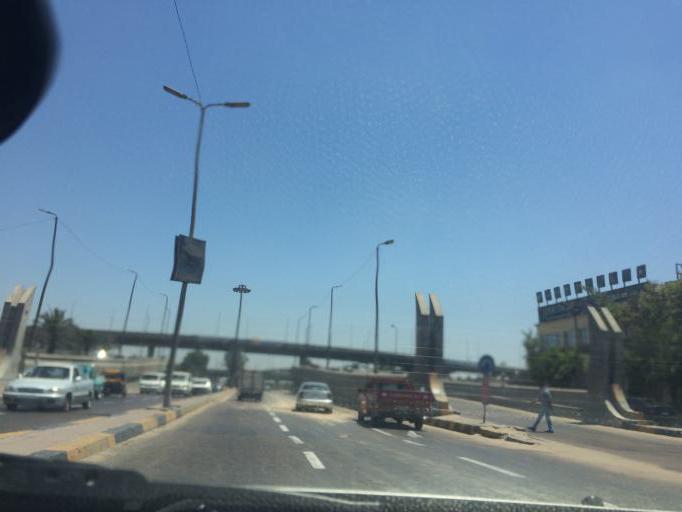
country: EG
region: Alexandria
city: Alexandria
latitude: 31.1831
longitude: 29.9269
